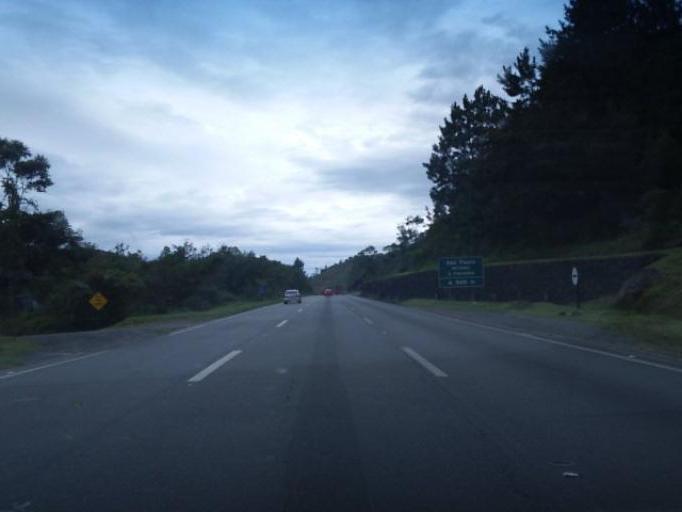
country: BR
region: Sao Paulo
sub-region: Cajati
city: Cajati
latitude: -24.9812
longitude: -48.5063
